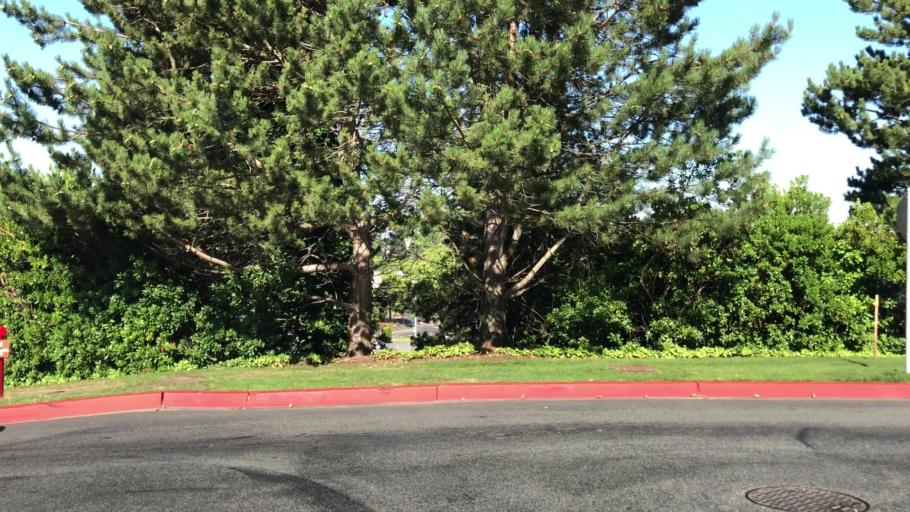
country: US
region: Washington
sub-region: King County
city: Newport
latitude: 47.5763
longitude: -122.1676
